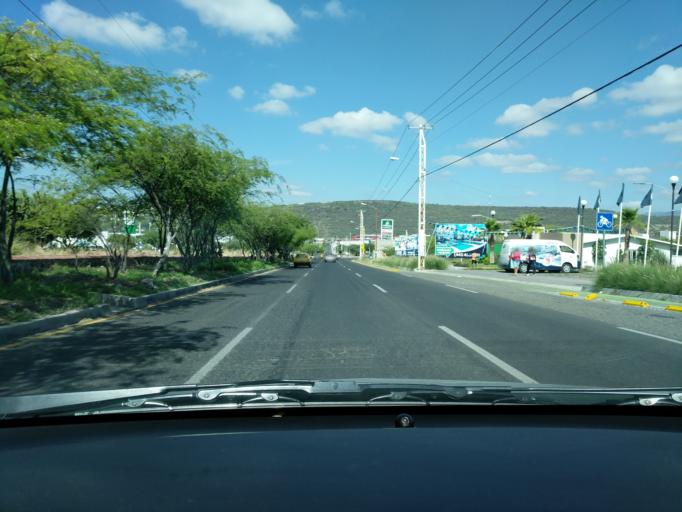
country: MX
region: Queretaro
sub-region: Queretaro
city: Patria Nueva
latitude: 20.6431
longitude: -100.4901
